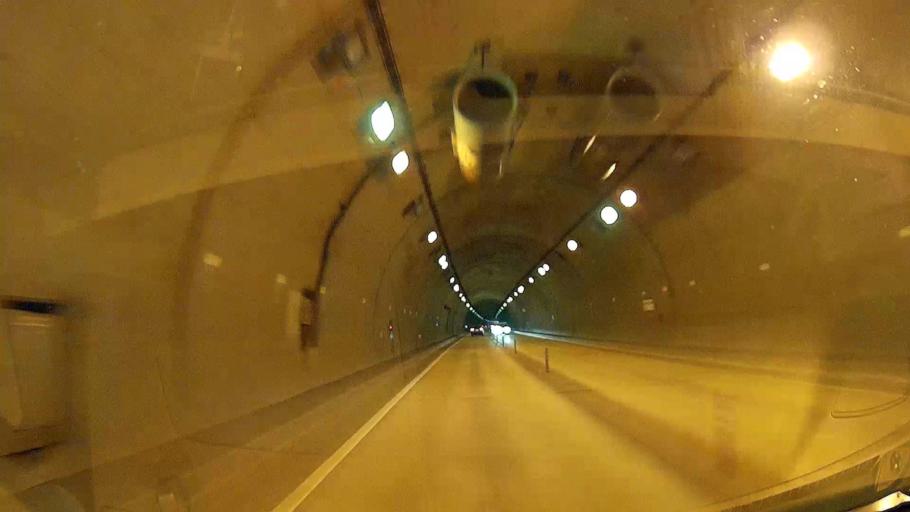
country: JP
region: Shizuoka
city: Shizuoka-shi
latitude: 35.0230
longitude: 138.3850
